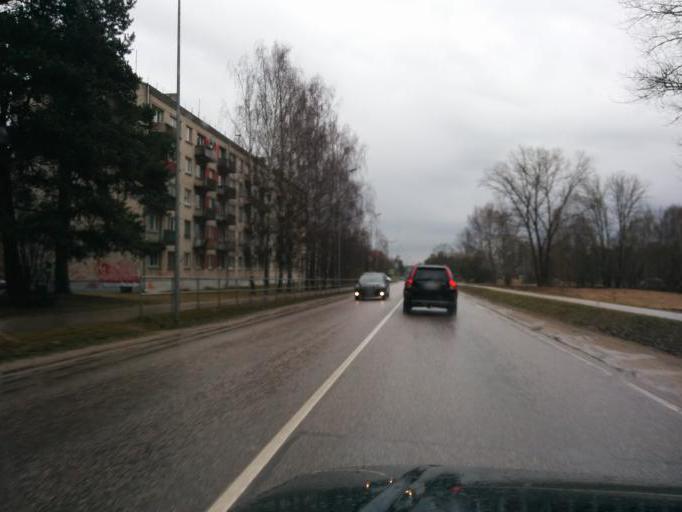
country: LV
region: Kekava
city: Balozi
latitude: 56.9054
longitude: 24.1463
